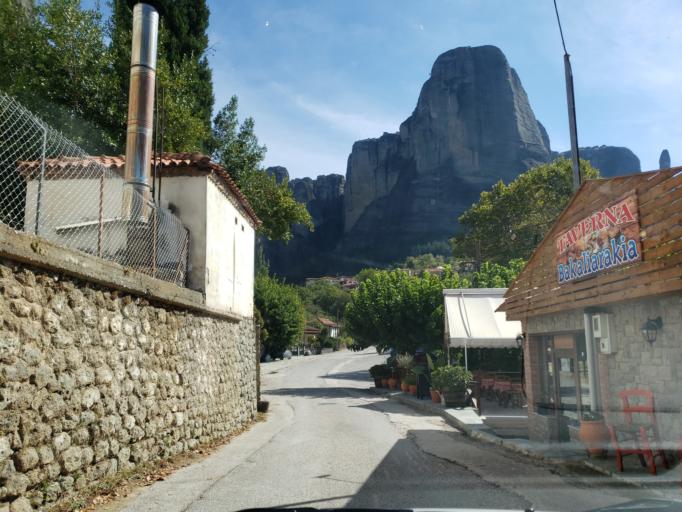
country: GR
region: Thessaly
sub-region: Trikala
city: Kastraki
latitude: 39.7165
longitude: 21.6205
